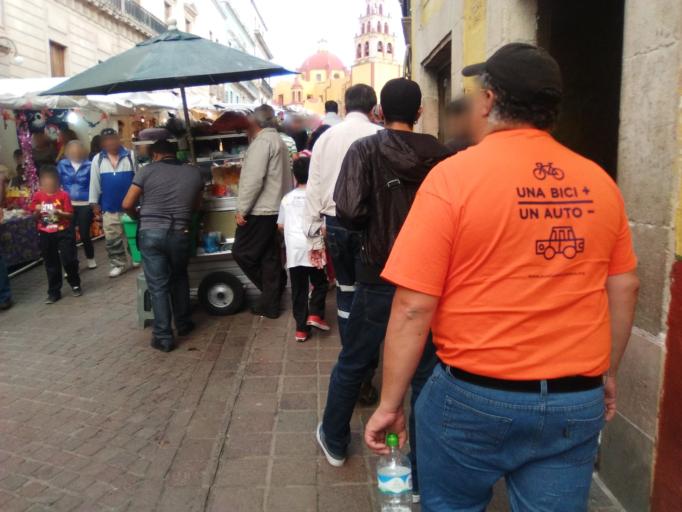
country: MX
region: Guanajuato
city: Guanajuato
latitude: 21.0172
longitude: -101.2548
